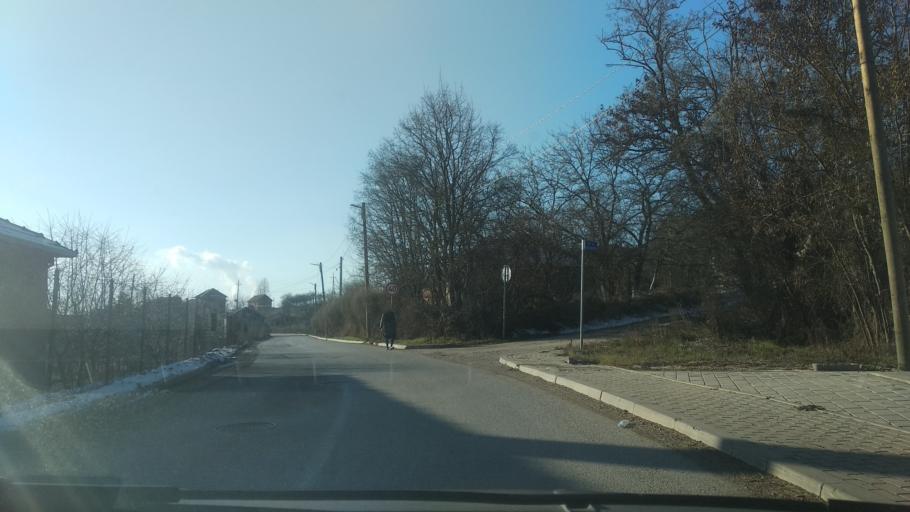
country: XK
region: Pristina
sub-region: Komuna e Prishtines
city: Pristina
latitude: 42.7158
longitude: 21.1676
